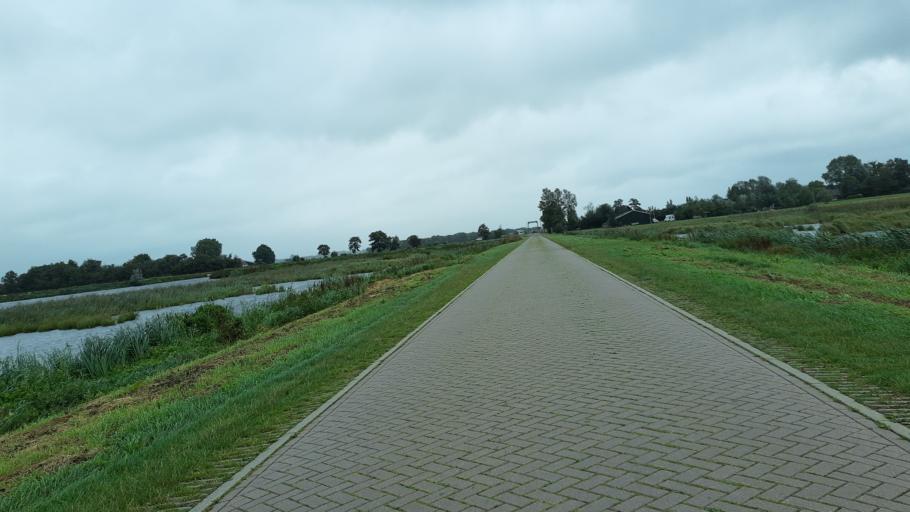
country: NL
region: Overijssel
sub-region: Gemeente Steenwijkerland
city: Blokzijl
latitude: 52.7548
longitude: 5.9897
